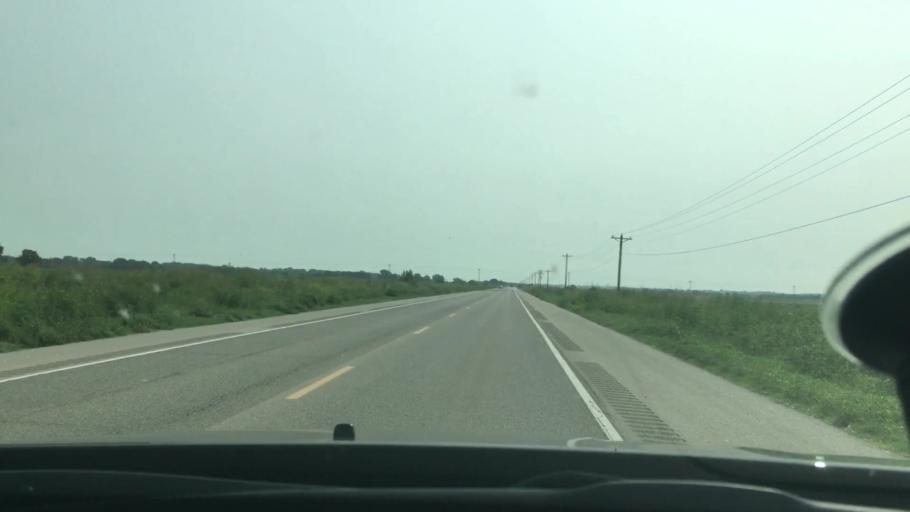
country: US
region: Oklahoma
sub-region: Garvin County
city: Lindsay
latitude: 34.8219
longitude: -97.5156
